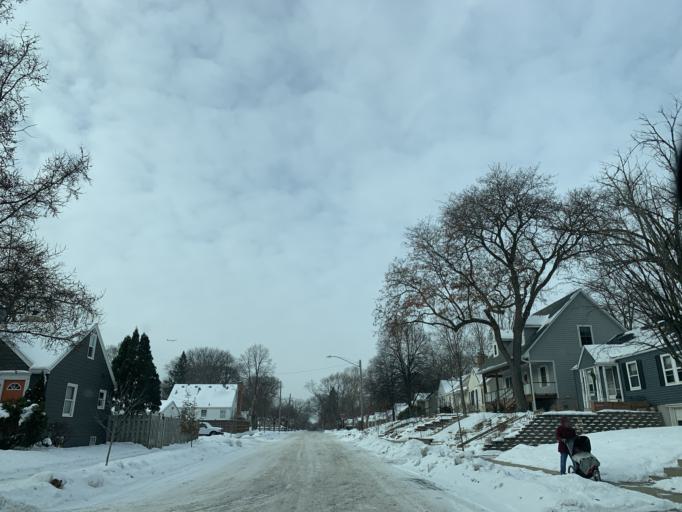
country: US
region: Minnesota
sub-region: Hennepin County
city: Richfield
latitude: 44.9036
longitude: -93.2139
